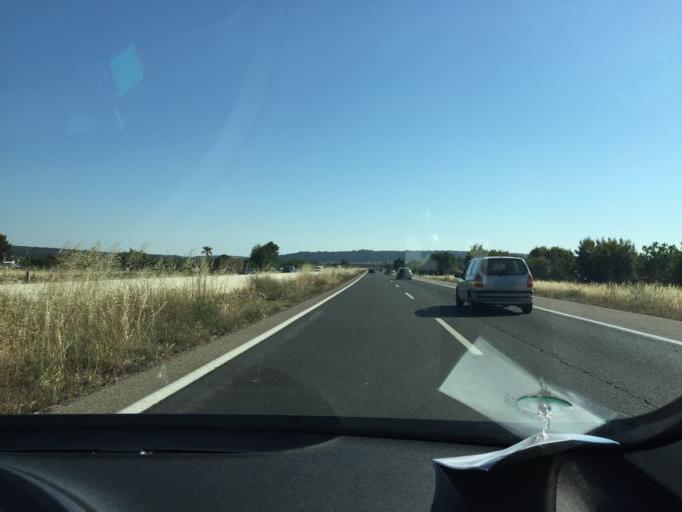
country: ES
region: Balearic Islands
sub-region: Illes Balears
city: Consell
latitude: 39.6561
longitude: 2.8027
